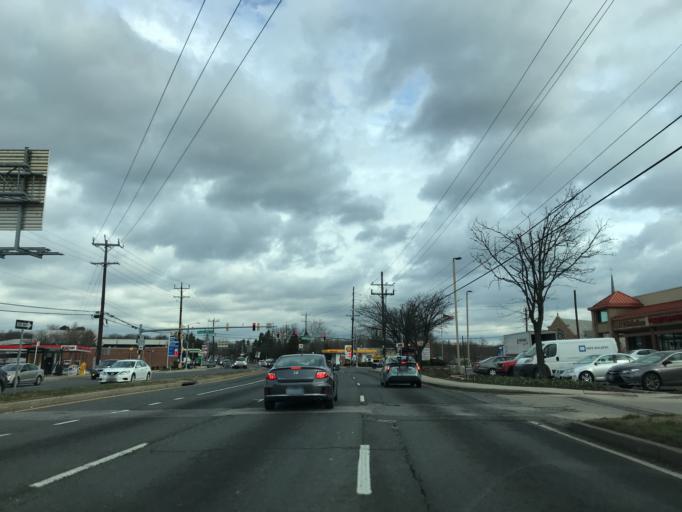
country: US
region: Maryland
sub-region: Montgomery County
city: Hillandale
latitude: 39.0213
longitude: -76.9768
